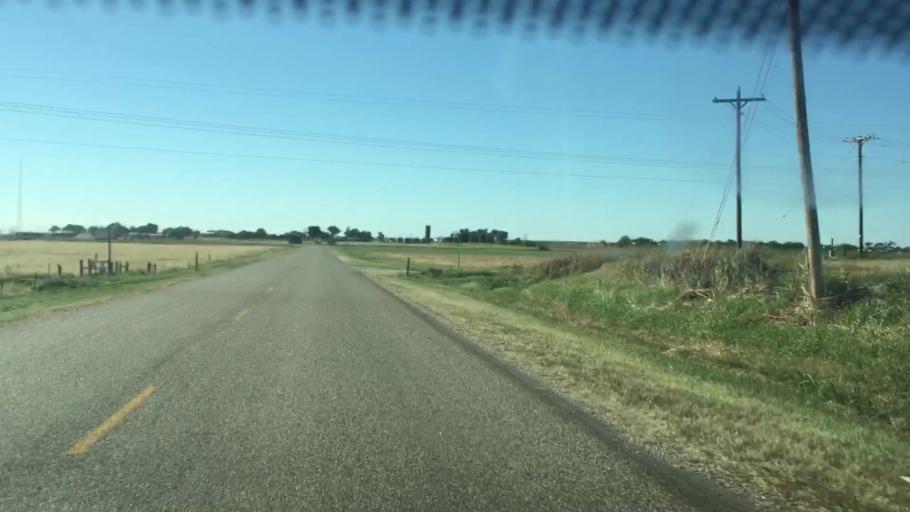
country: US
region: Colorado
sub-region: Prowers County
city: Lamar
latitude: 38.1170
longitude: -102.6036
